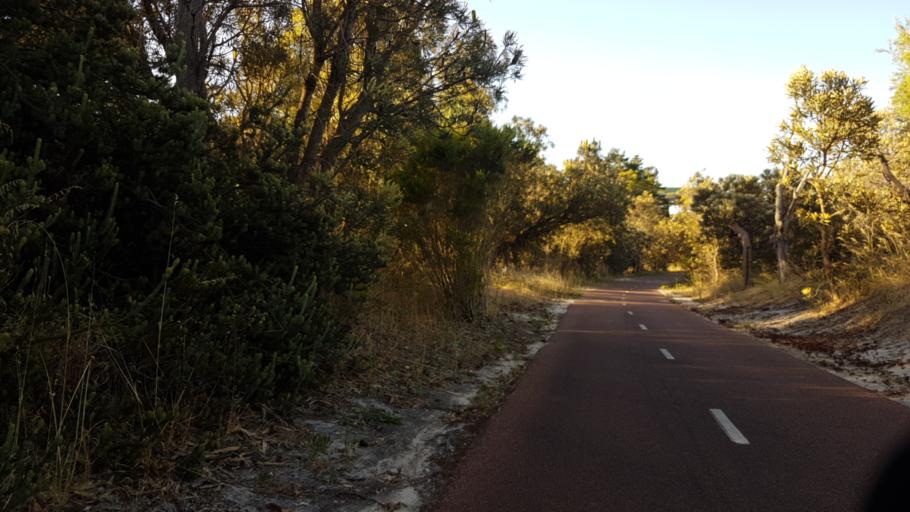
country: AU
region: Western Australia
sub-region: Kwinana
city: Bertram
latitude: -32.2297
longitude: 115.8489
